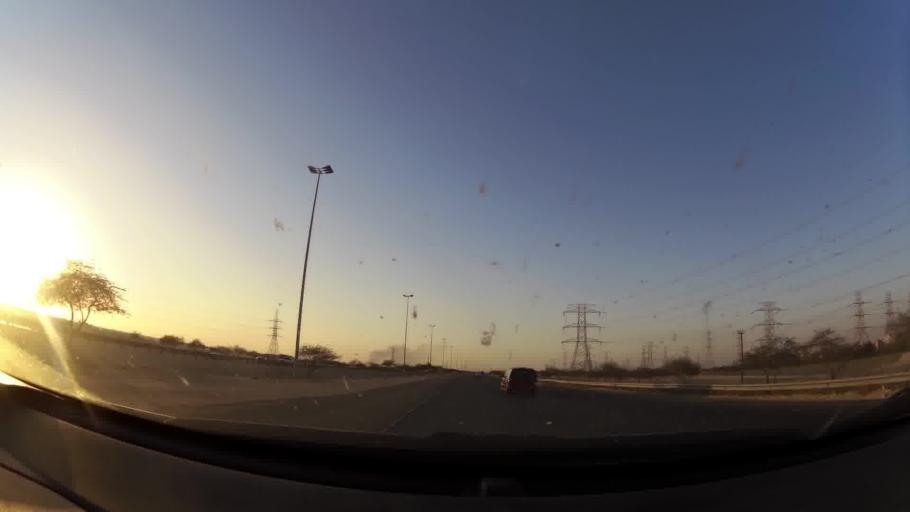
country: KW
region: Al Ahmadi
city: Al Fahahil
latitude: 28.9429
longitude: 48.1441
